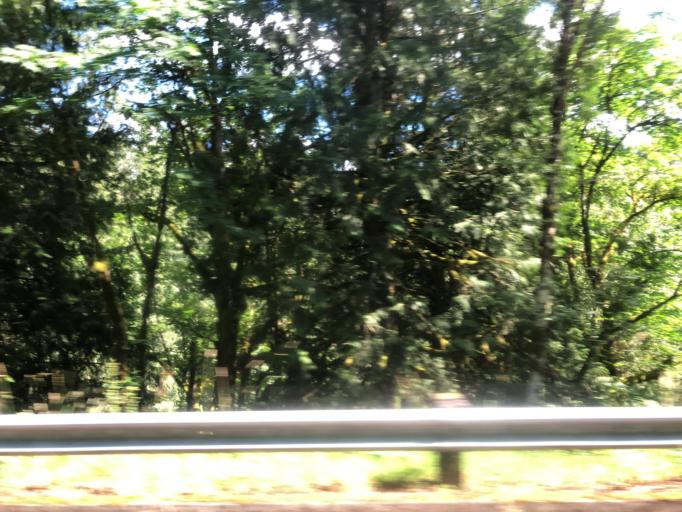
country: US
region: Oregon
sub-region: Clackamas County
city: Sandy
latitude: 45.4258
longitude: -122.2215
